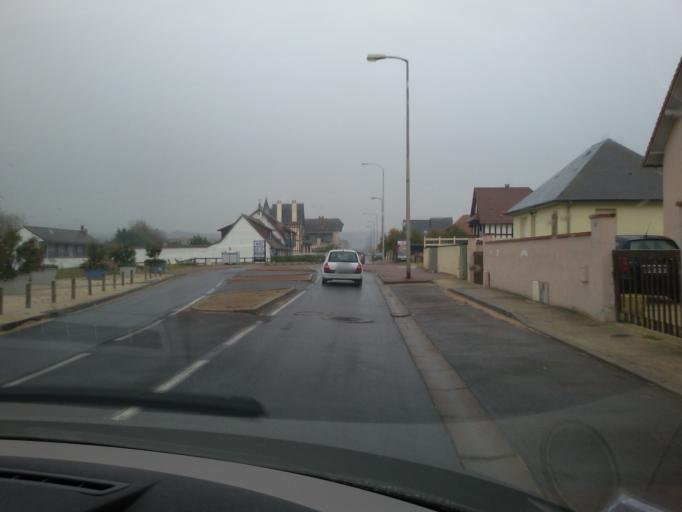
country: FR
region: Lower Normandy
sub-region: Departement du Calvados
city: Blonville-sur-Mer
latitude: 49.3336
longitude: 0.0170
